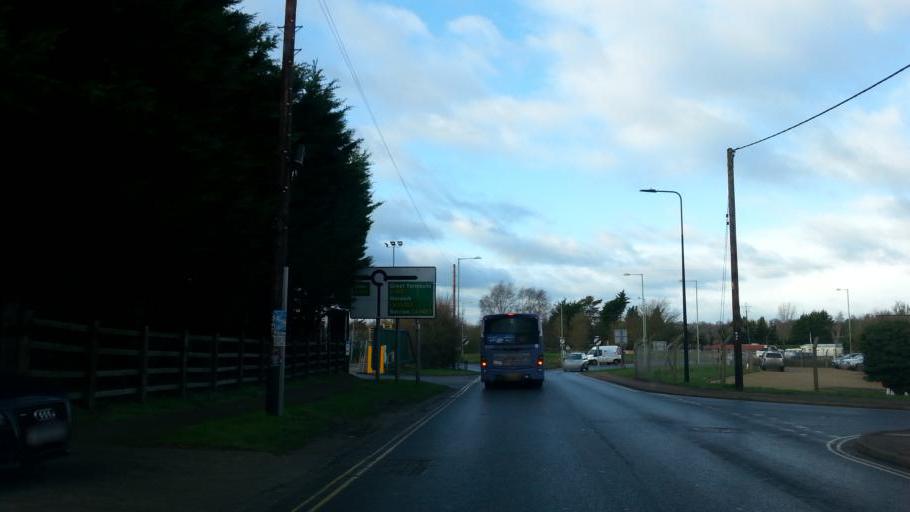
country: GB
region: England
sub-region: Suffolk
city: Bungay
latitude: 52.4588
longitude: 1.4340
